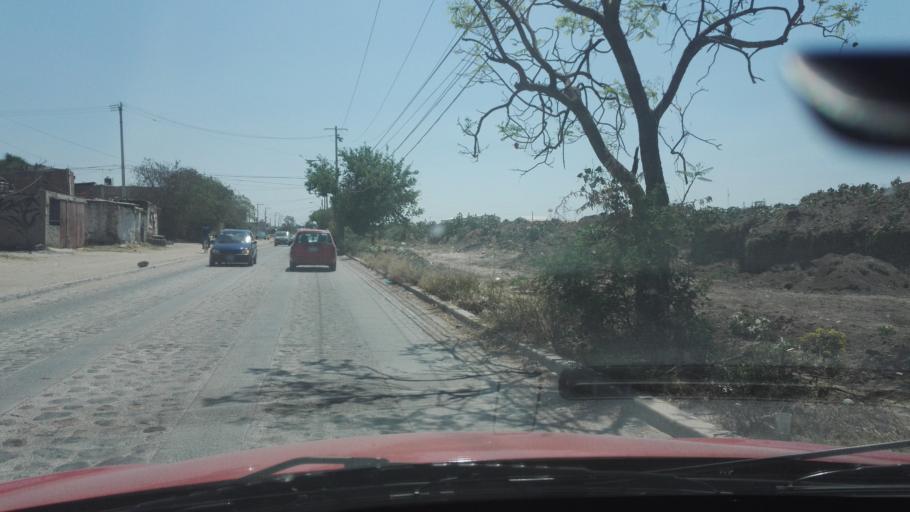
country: MX
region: Guanajuato
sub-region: Leon
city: Fraccionamiento Paraiso Real
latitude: 21.0930
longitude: -101.5986
